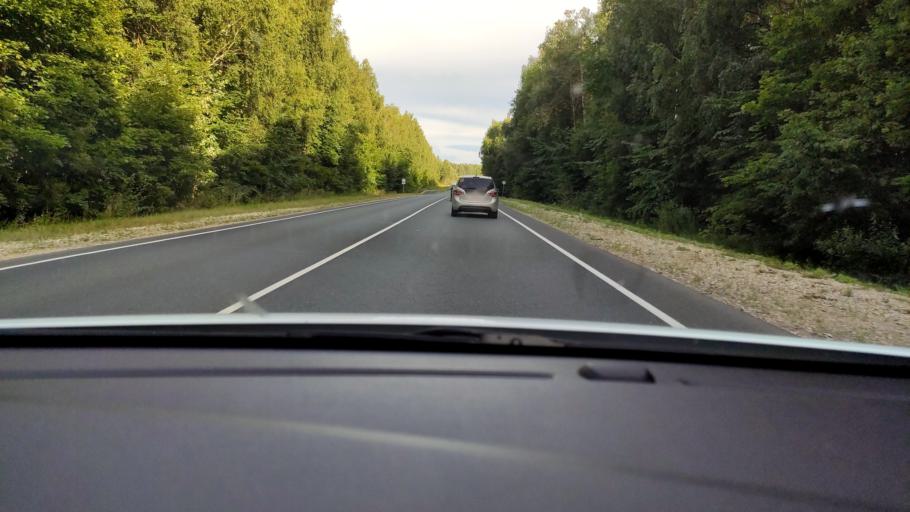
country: RU
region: Mariy-El
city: Krasnogorskiy
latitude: 56.1836
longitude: 48.2580
